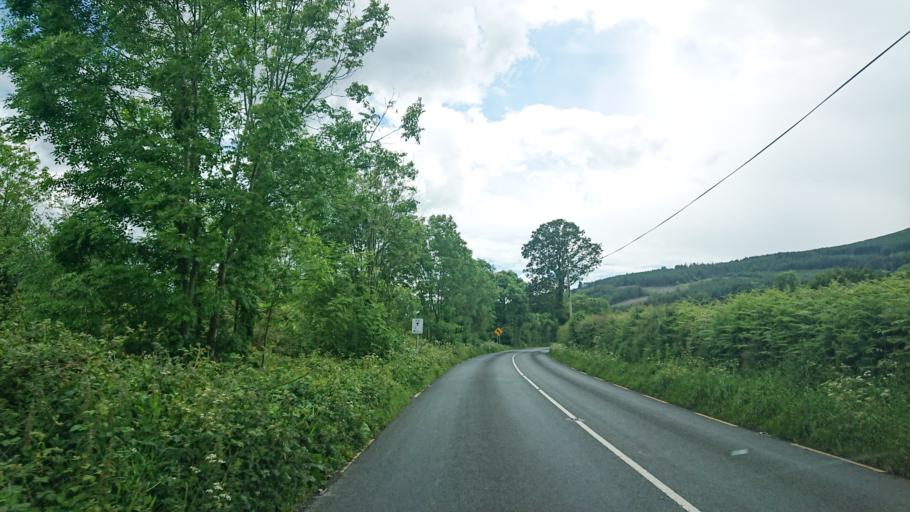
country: IE
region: Leinster
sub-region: Kilkenny
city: Graiguenamanagh
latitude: 52.5275
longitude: -6.9532
